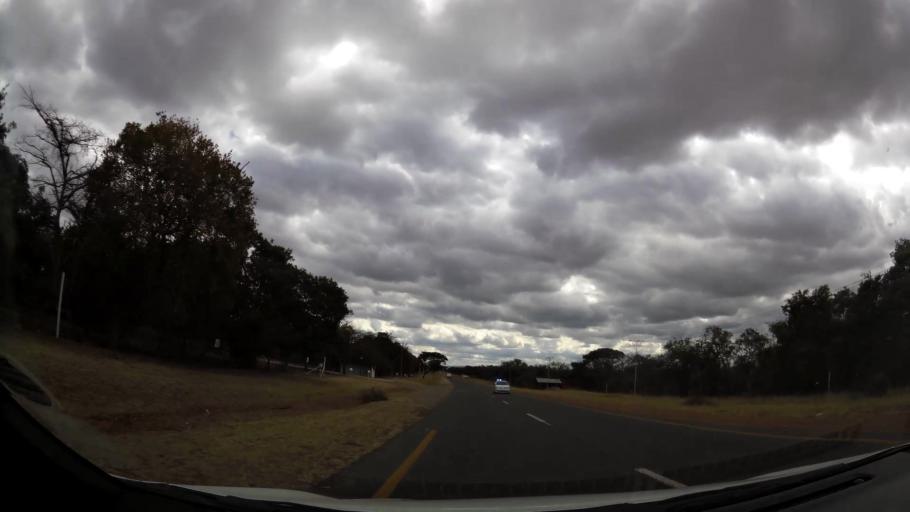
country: ZA
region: Limpopo
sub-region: Waterberg District Municipality
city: Modimolle
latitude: -24.7723
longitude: 28.4698
